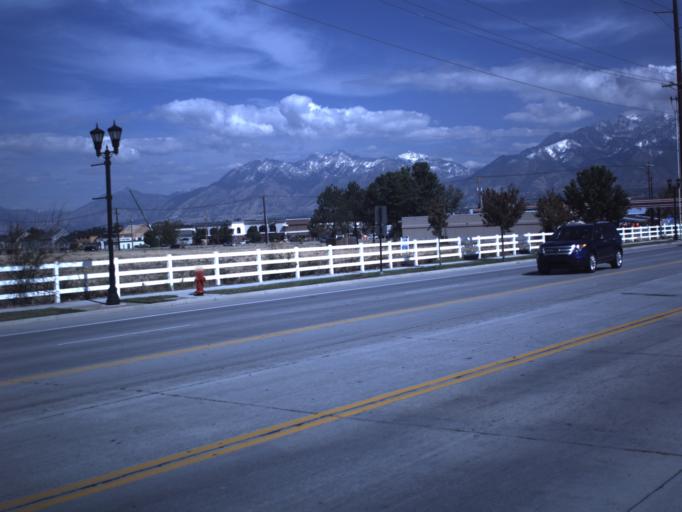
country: US
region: Utah
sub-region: Salt Lake County
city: South Jordan
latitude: 40.5441
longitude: -111.9410
